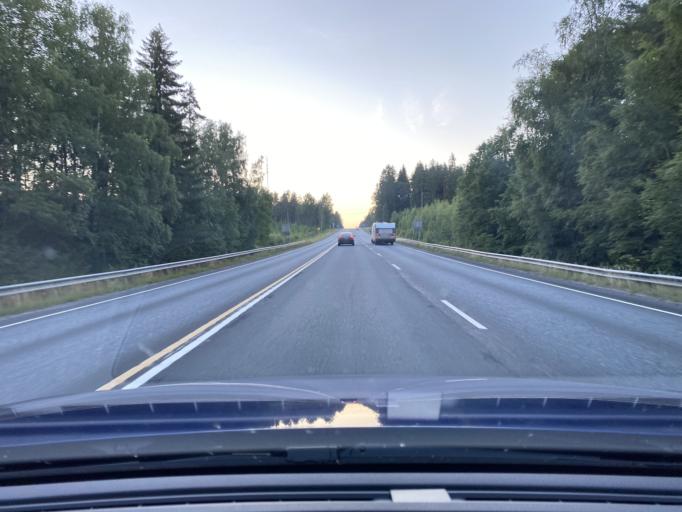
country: FI
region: Pirkanmaa
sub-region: Luoteis-Pirkanmaa
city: Ikaalinen
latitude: 61.7781
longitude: 23.0044
